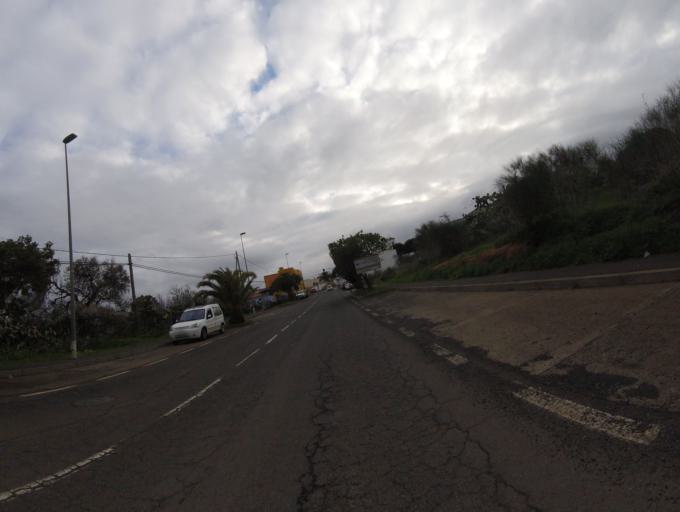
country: ES
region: Canary Islands
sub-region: Provincia de Santa Cruz de Tenerife
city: La Laguna
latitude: 28.4432
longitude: -16.3340
